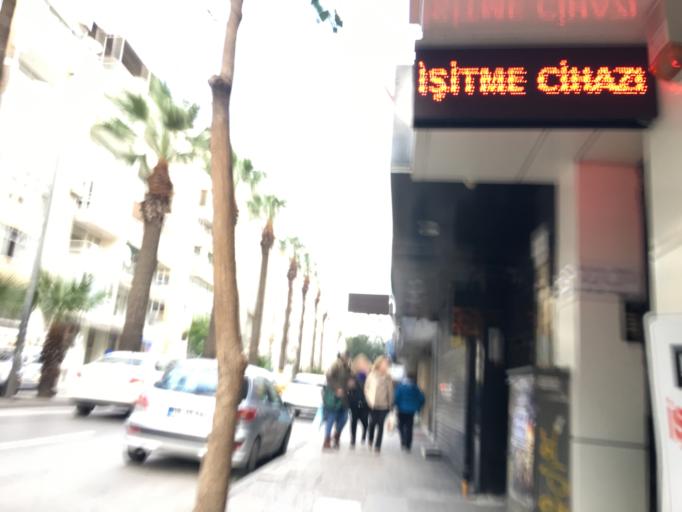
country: TR
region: Izmir
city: Izmir
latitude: 38.4348
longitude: 27.1430
